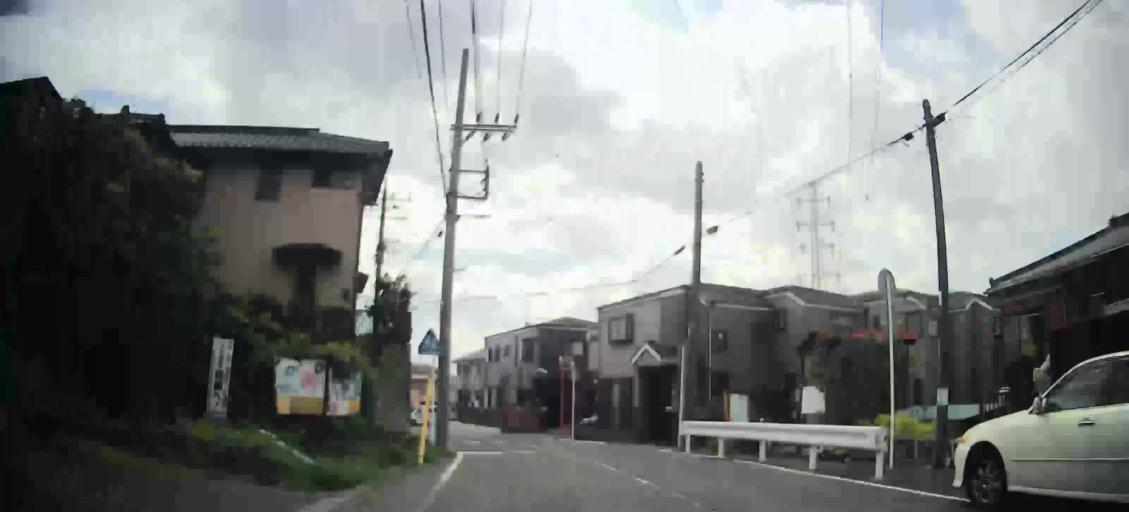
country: JP
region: Kanagawa
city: Yokohama
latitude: 35.4845
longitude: 139.5512
